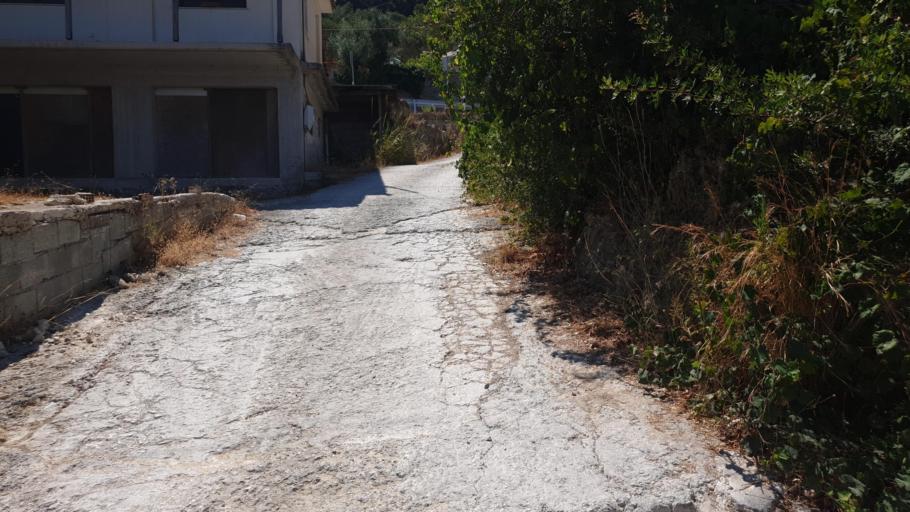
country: GR
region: Ionian Islands
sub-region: Nomos Zakynthou
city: Zakynthos
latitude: 37.7467
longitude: 20.9449
